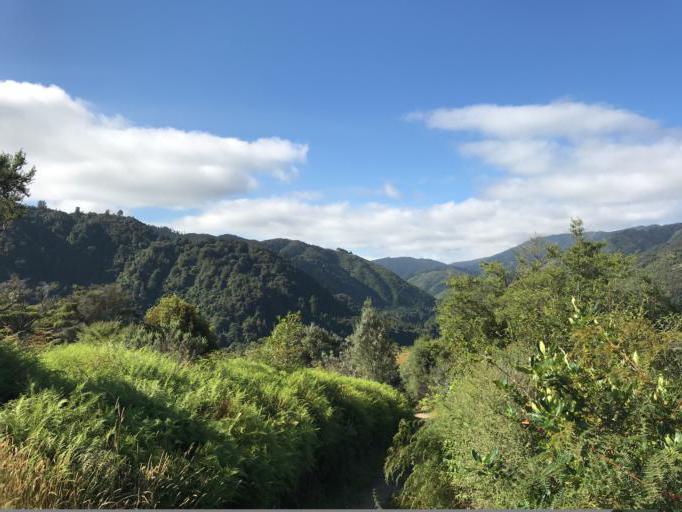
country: NZ
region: Wellington
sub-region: Kapiti Coast District
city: Otaki
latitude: -40.8765
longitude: 175.2346
